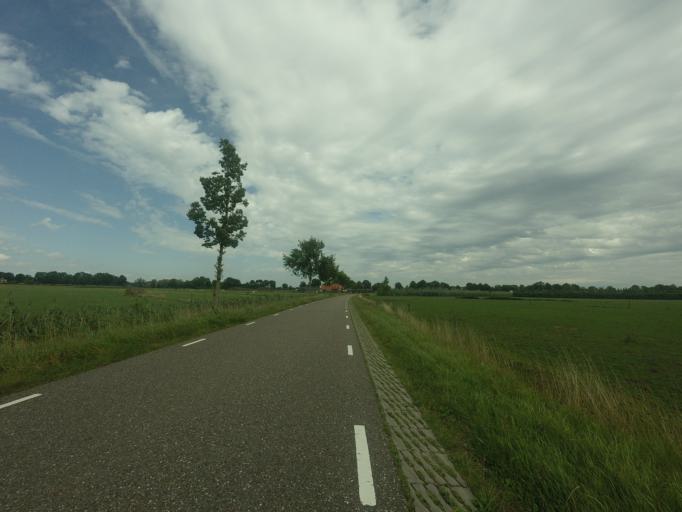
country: NL
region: Overijssel
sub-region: Gemeente Dalfsen
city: Dalfsen
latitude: 52.4730
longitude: 6.3616
